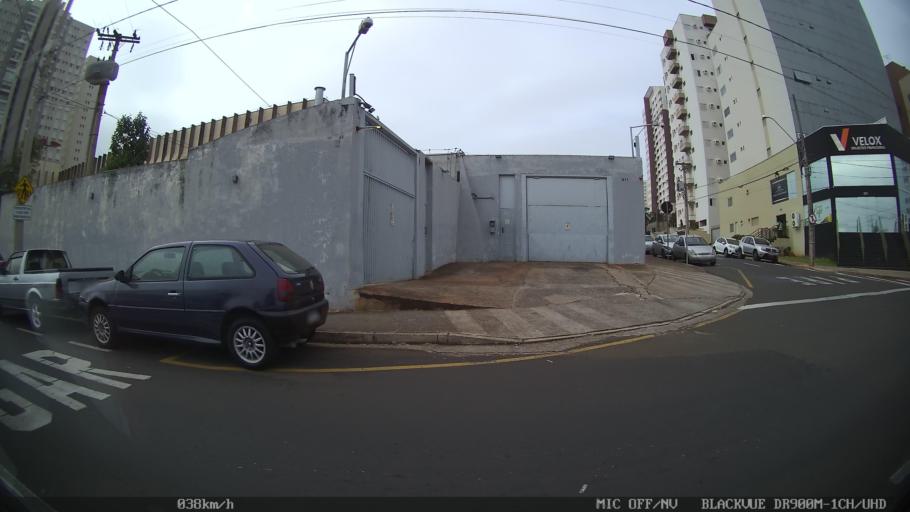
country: BR
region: Sao Paulo
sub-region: Sao Jose Do Rio Preto
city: Sao Jose do Rio Preto
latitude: -20.8263
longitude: -49.3835
